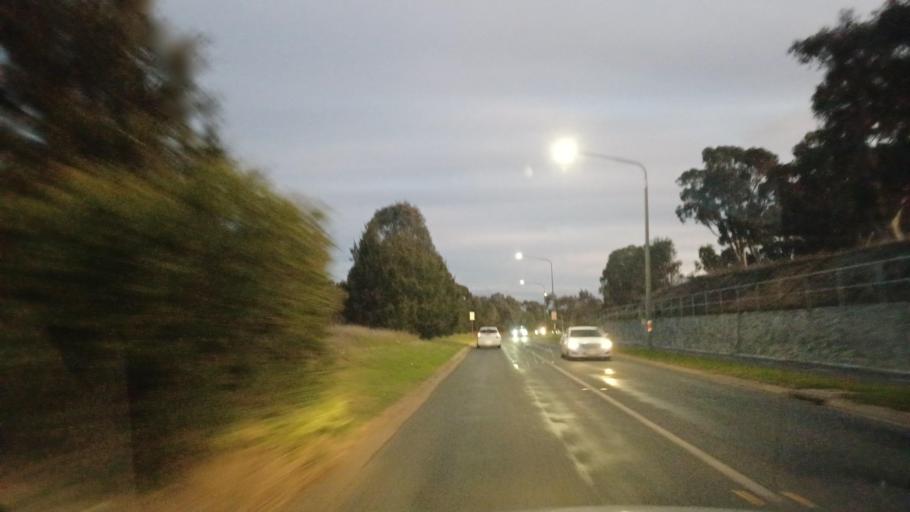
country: AU
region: Australian Capital Territory
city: Belconnen
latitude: -35.1894
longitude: 149.0715
